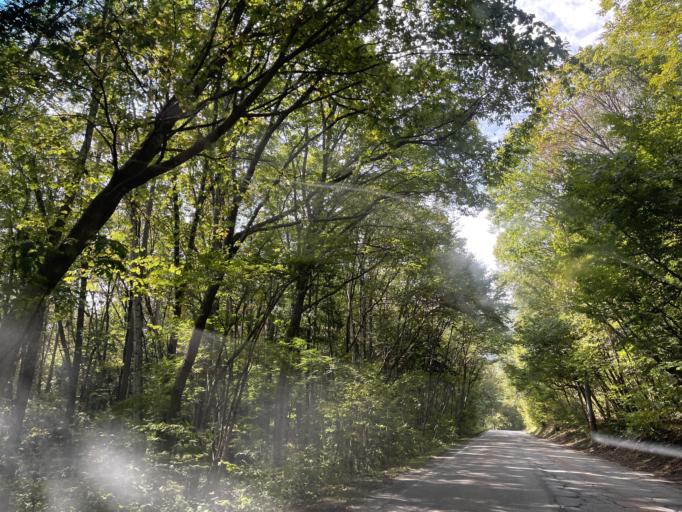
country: JP
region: Nagano
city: Omachi
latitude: 36.5208
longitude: 137.7861
